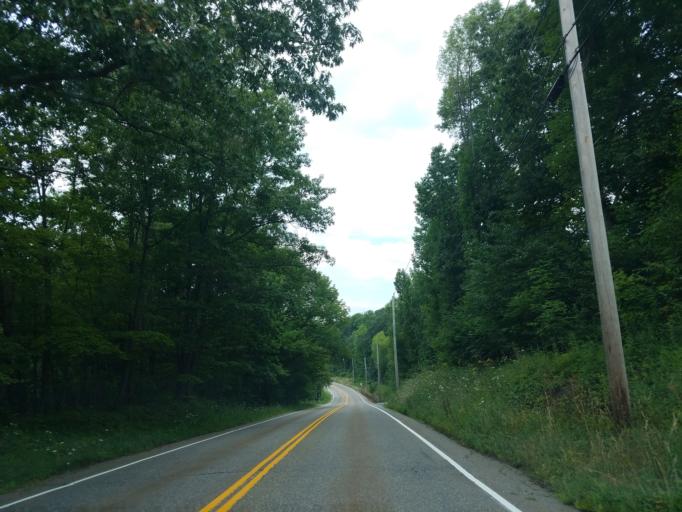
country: US
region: Connecticut
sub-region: Litchfield County
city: New Preston
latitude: 41.7735
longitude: -73.3530
